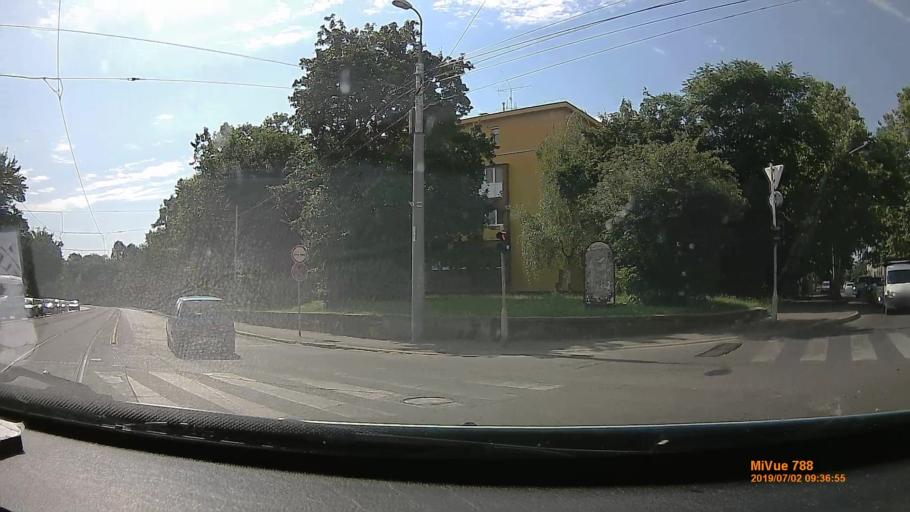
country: HU
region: Borsod-Abauj-Zemplen
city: Miskolc
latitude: 48.1028
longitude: 20.7981
